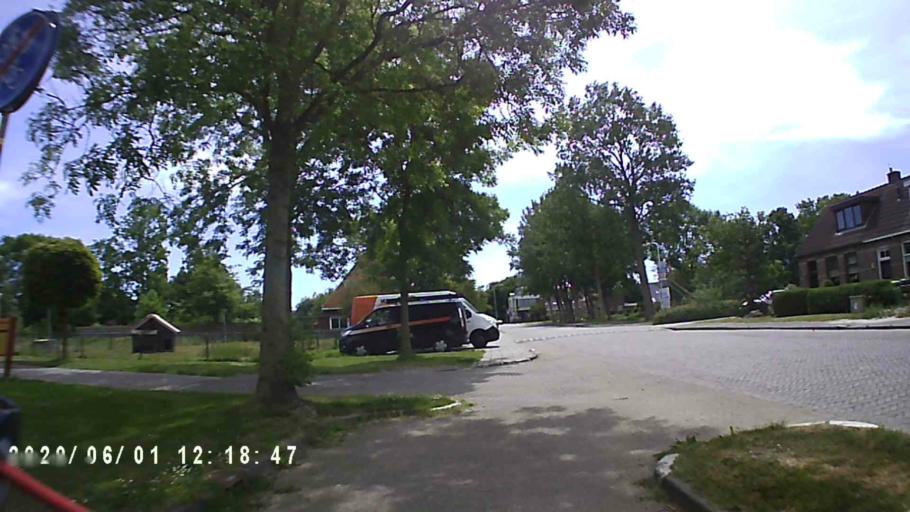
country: NL
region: Friesland
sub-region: Gemeente Harlingen
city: Harlingen
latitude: 53.1318
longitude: 5.4729
